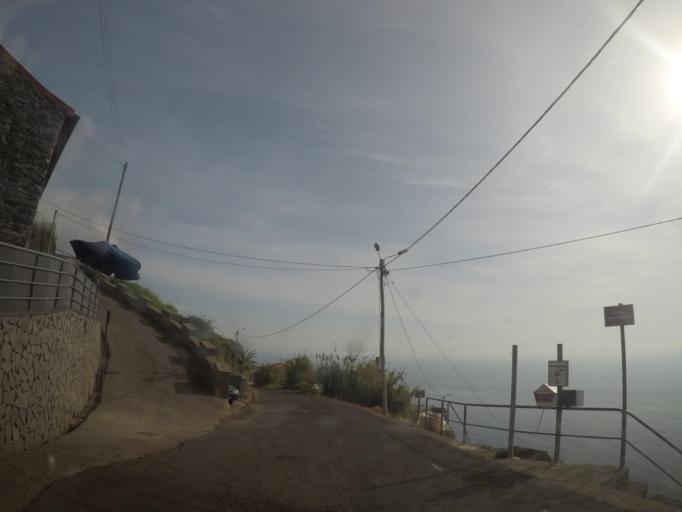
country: PT
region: Madeira
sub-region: Calheta
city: Faja da Ovelha
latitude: 32.7752
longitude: -17.2376
